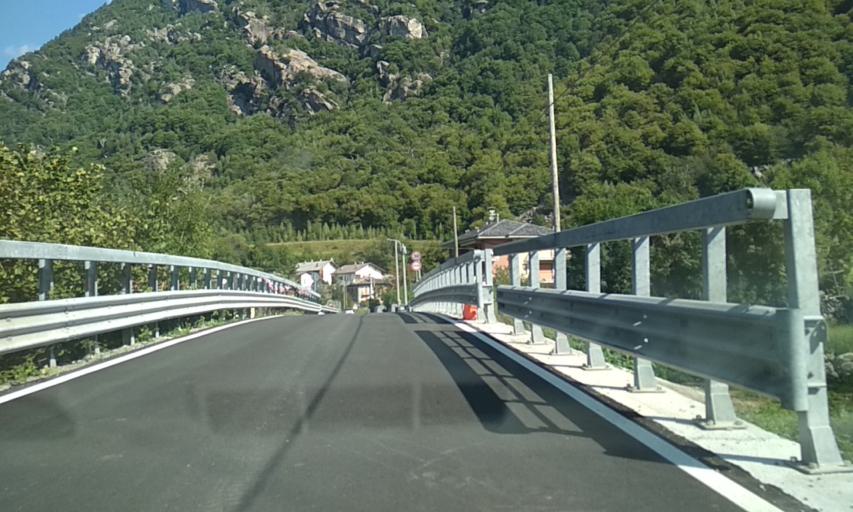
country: IT
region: Piedmont
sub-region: Provincia di Torino
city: Locana
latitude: 45.4287
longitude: 7.4350
